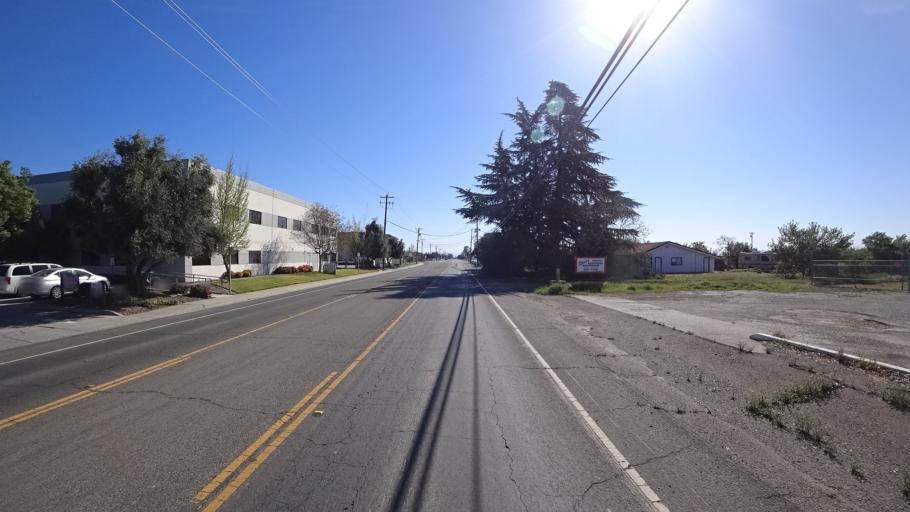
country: US
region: California
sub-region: Glenn County
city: Orland
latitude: 39.7472
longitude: -122.1751
